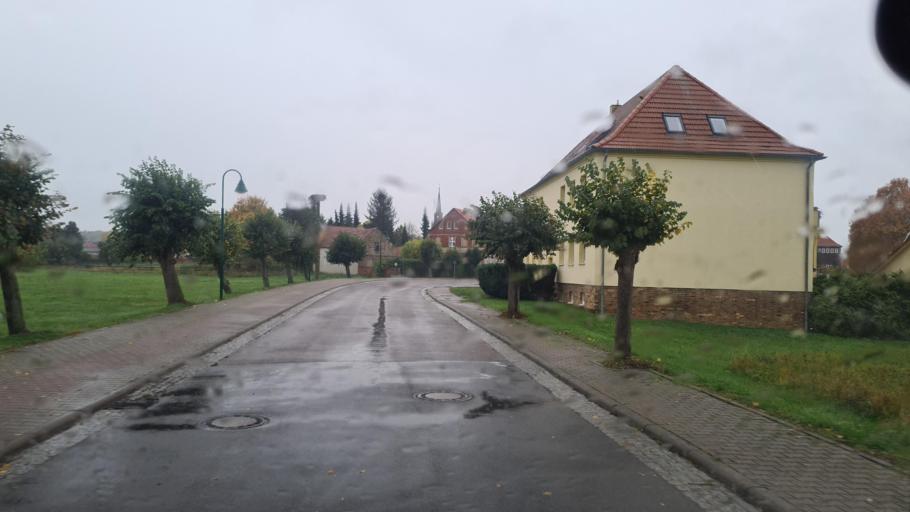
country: DE
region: Brandenburg
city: Schlieben
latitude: 51.7274
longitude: 13.3822
